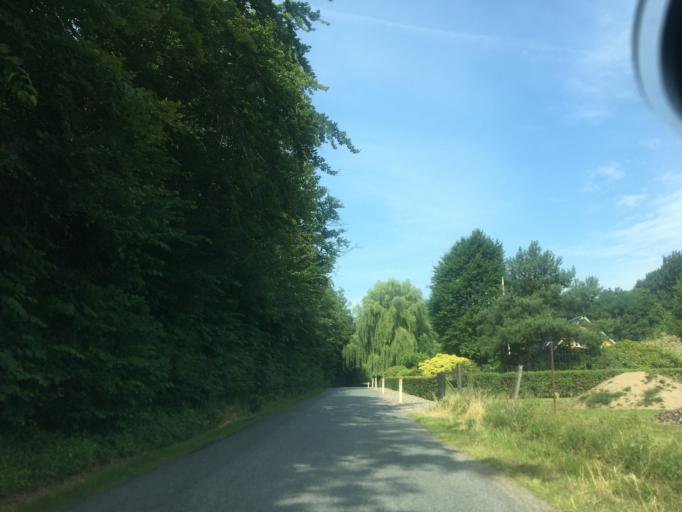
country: DK
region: Zealand
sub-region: Faxe Kommune
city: Fakse
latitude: 55.1939
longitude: 12.0662
